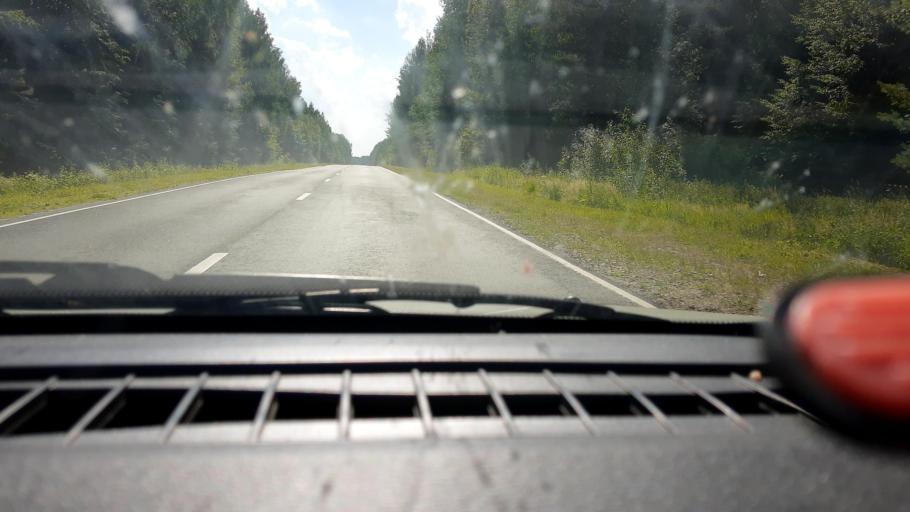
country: RU
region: Nizjnij Novgorod
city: Uren'
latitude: 57.2301
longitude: 45.5415
